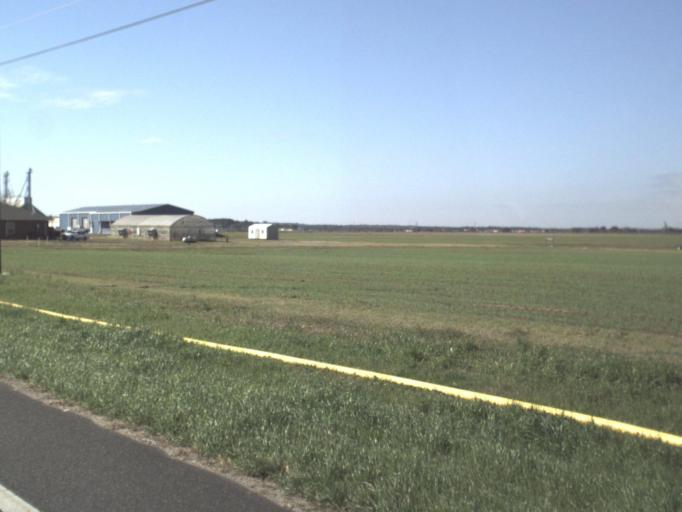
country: US
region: Florida
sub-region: Jackson County
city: Marianna
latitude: 30.8529
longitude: -85.1644
